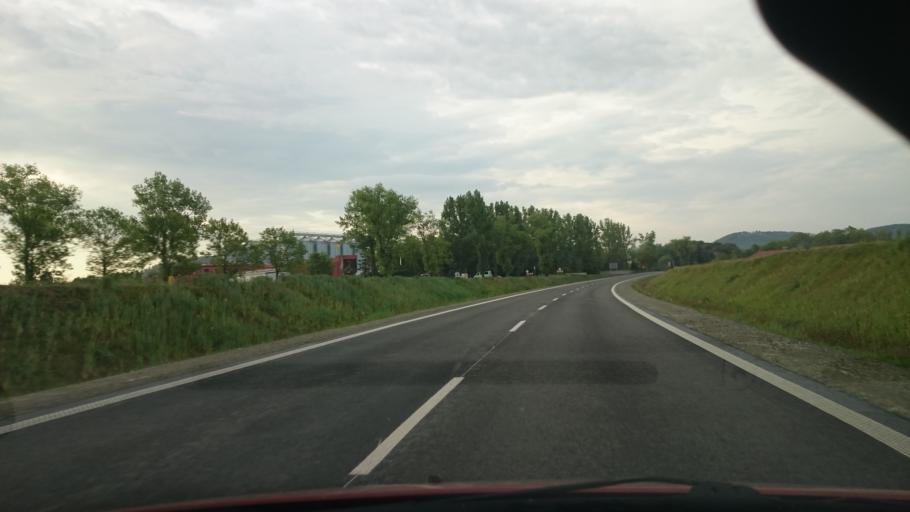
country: PL
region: Lower Silesian Voivodeship
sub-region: Powiat klodzki
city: Klodzko
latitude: 50.3943
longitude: 16.6581
